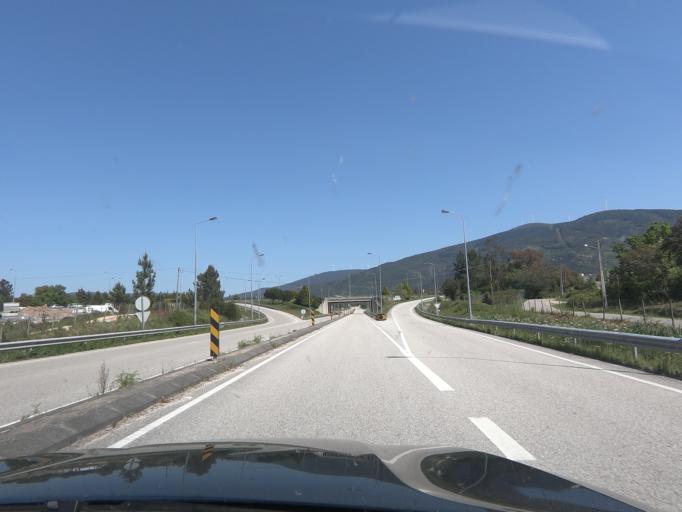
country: PT
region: Coimbra
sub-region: Lousa
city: Lousa
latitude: 40.1288
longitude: -8.2507
